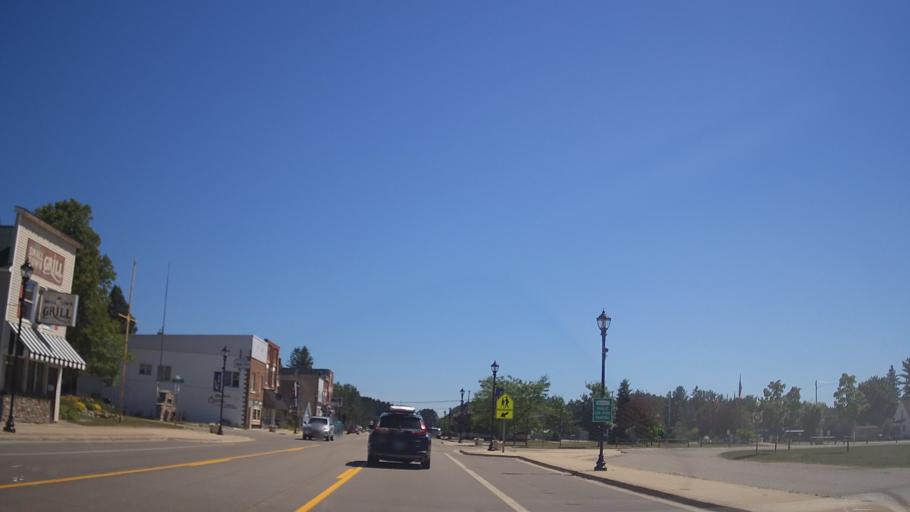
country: US
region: Michigan
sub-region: Cheboygan County
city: Indian River
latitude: 45.5540
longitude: -84.7844
